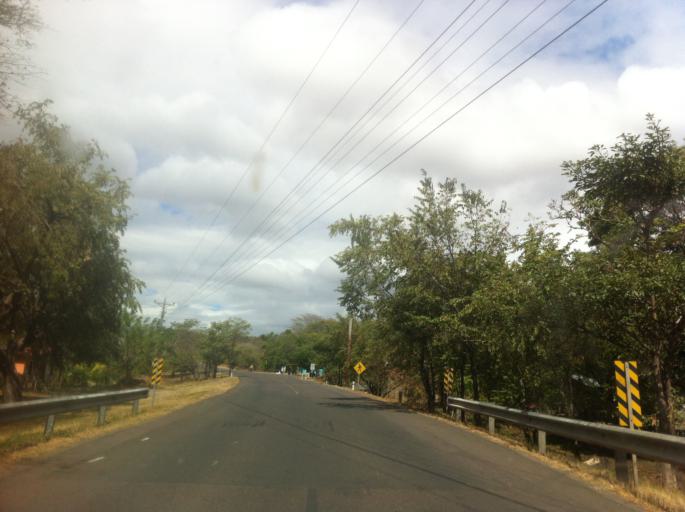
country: NI
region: Chontales
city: Juigalpa
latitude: 12.0440
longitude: -85.2808
